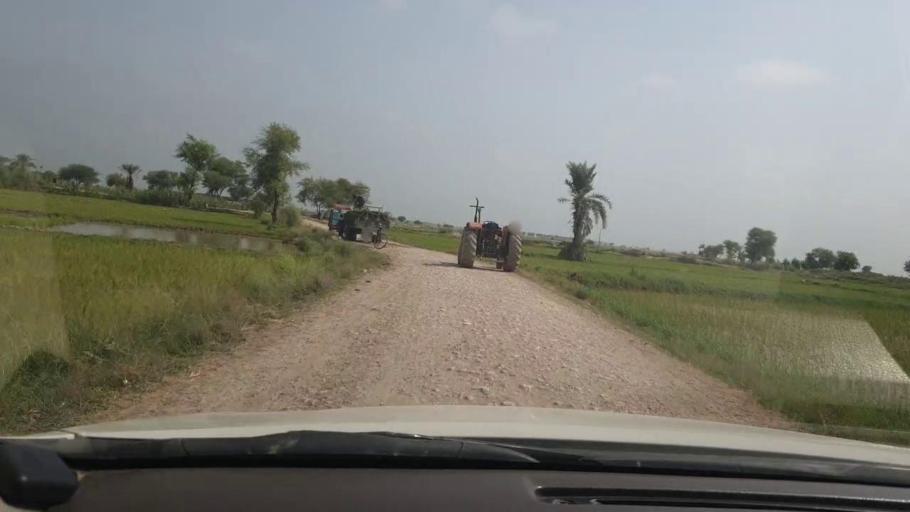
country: PK
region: Sindh
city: Shikarpur
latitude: 28.0137
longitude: 68.5945
